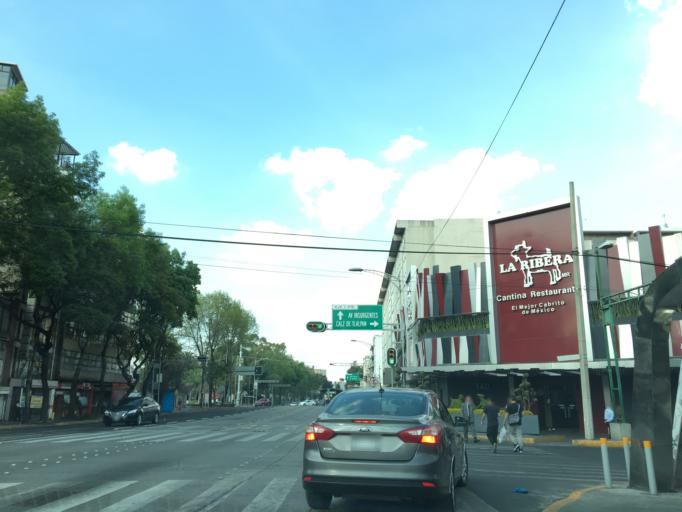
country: MX
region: Mexico City
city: Benito Juarez
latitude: 19.4184
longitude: -99.1542
